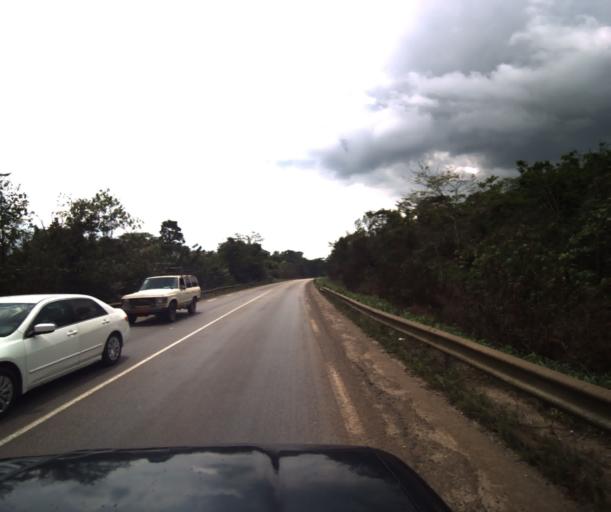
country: CM
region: Littoral
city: Dizangue
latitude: 3.9495
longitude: 10.0209
